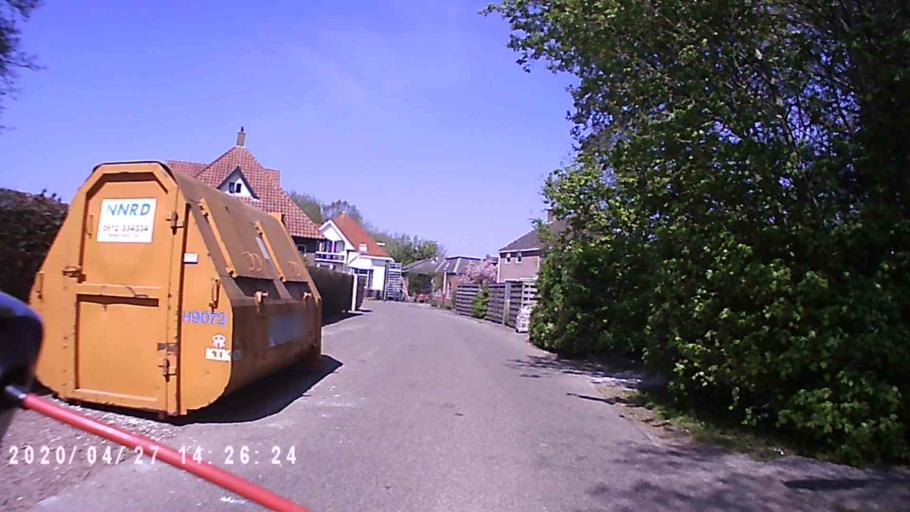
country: NL
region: Groningen
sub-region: Gemeente De Marne
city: Ulrum
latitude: 53.3869
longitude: 6.3952
